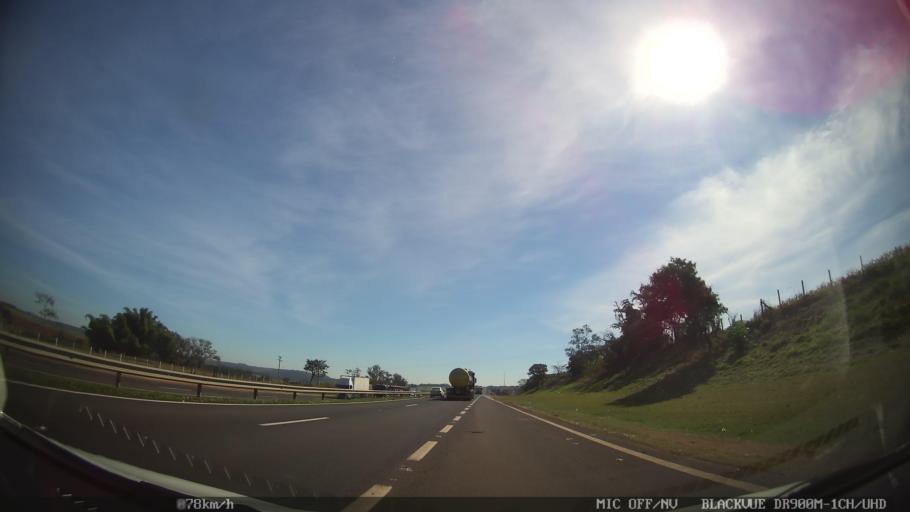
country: BR
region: Sao Paulo
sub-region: Pirassununga
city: Pirassununga
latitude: -22.0711
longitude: -47.4236
